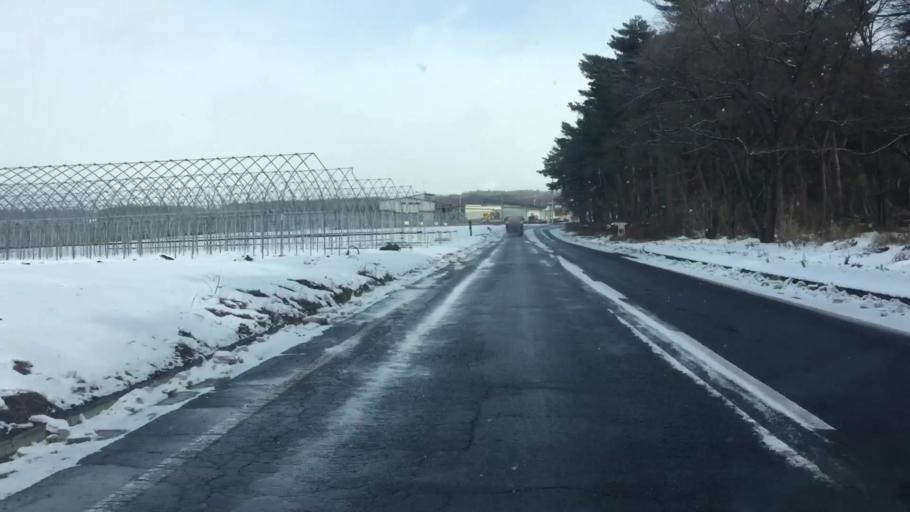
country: JP
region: Gunma
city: Numata
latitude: 36.6243
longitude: 139.0901
